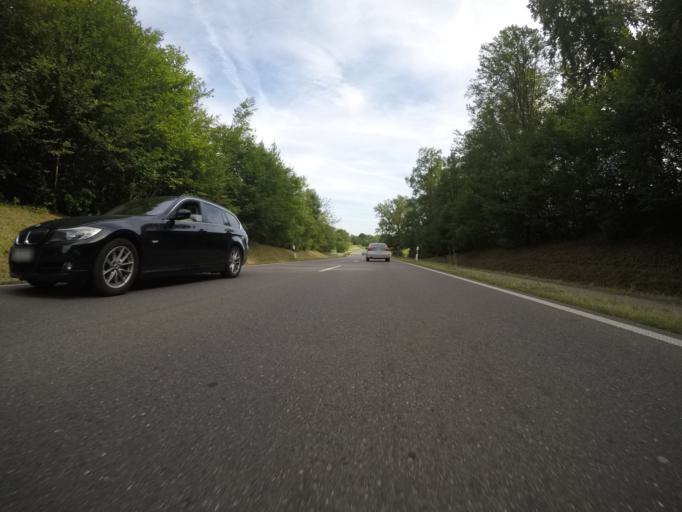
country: DE
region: Baden-Wuerttemberg
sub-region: Regierungsbezirk Stuttgart
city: Renningen
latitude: 48.7845
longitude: 8.9299
